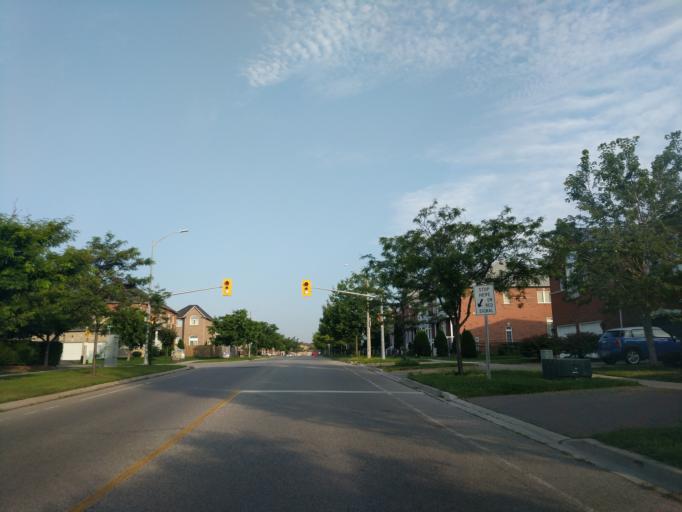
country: CA
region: Ontario
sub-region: York
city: Richmond Hill
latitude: 43.8847
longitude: -79.4043
